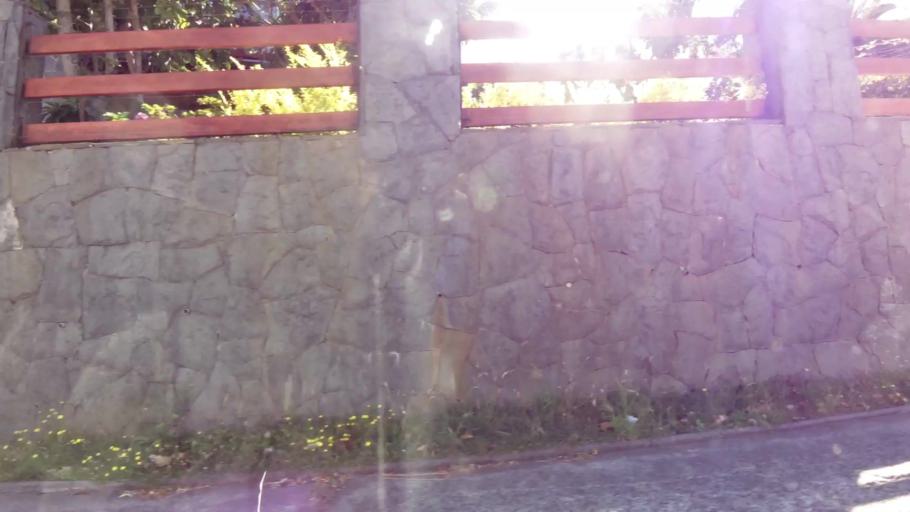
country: CL
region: Biobio
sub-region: Provincia de Concepcion
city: Concepcion
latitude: -36.7937
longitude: -73.0595
